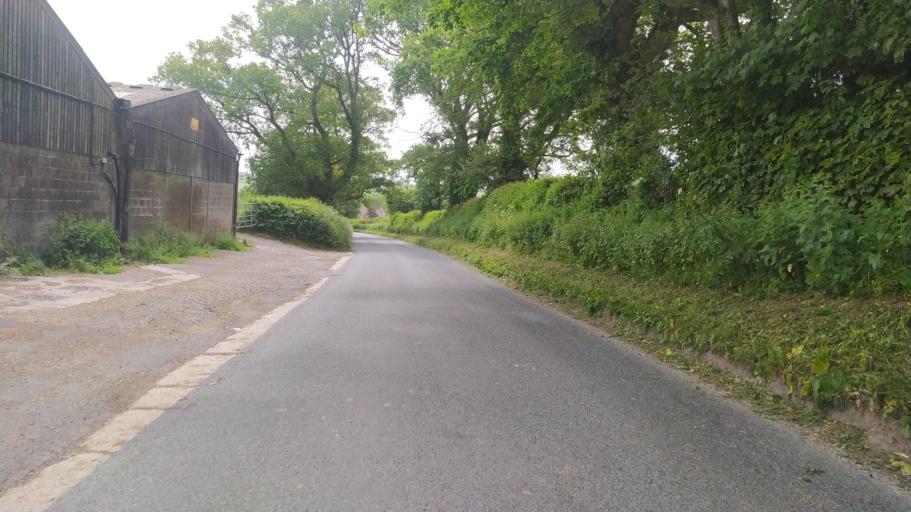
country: GB
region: England
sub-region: Somerset
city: Yeovil
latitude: 50.8379
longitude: -2.5840
